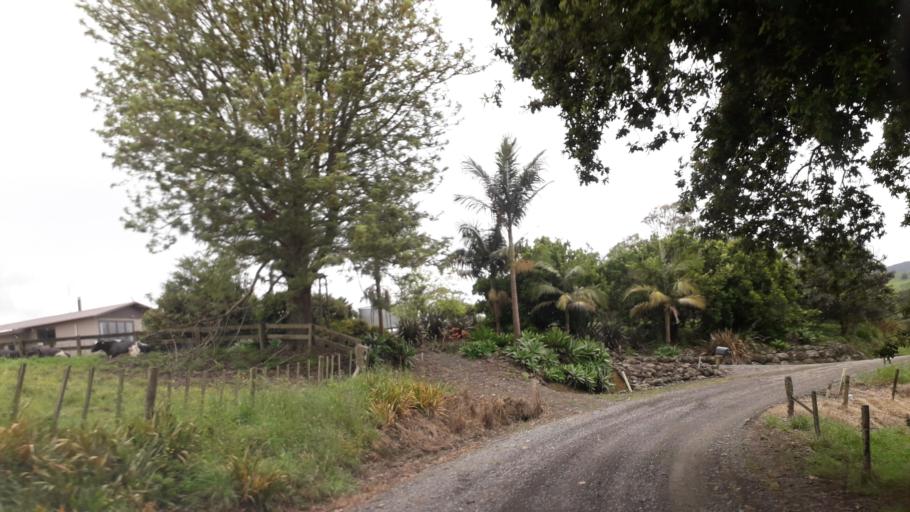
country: NZ
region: Northland
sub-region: Far North District
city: Waimate North
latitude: -35.3002
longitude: 173.5646
